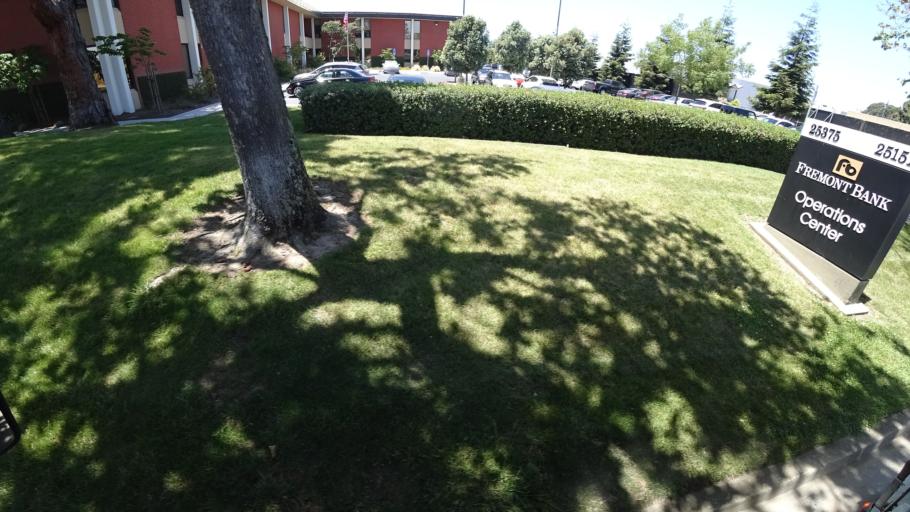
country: US
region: California
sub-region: Alameda County
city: San Lorenzo
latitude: 37.6369
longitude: -122.1199
